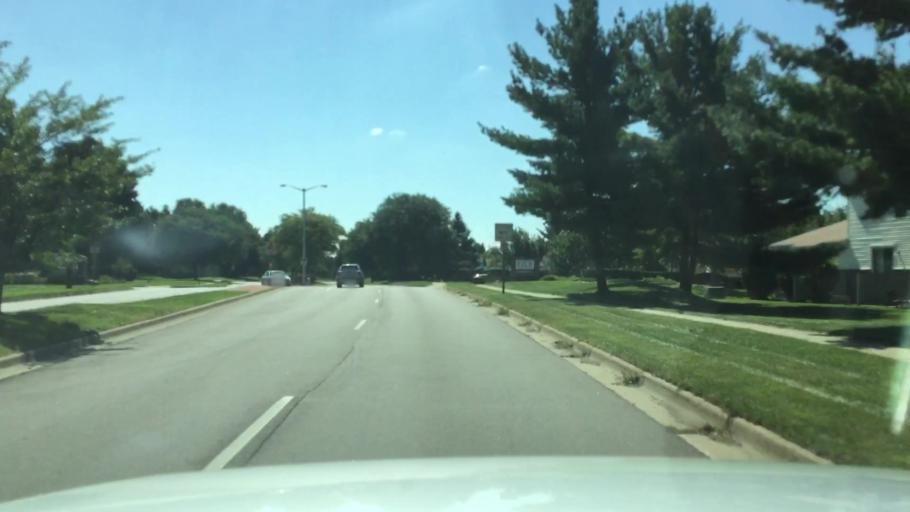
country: US
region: Michigan
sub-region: Kalamazoo County
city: Portage
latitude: 42.2279
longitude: -85.6017
